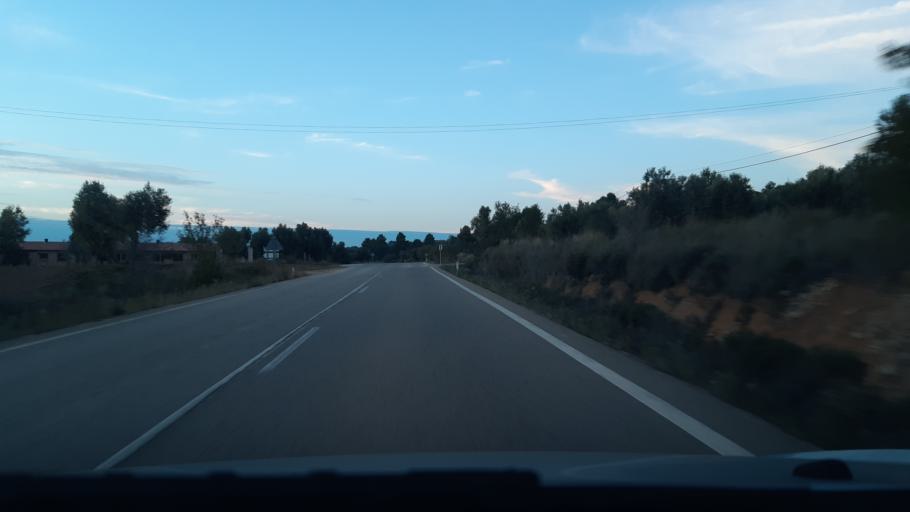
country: ES
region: Aragon
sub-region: Provincia de Teruel
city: Valderrobres
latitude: 40.8529
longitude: 0.1734
